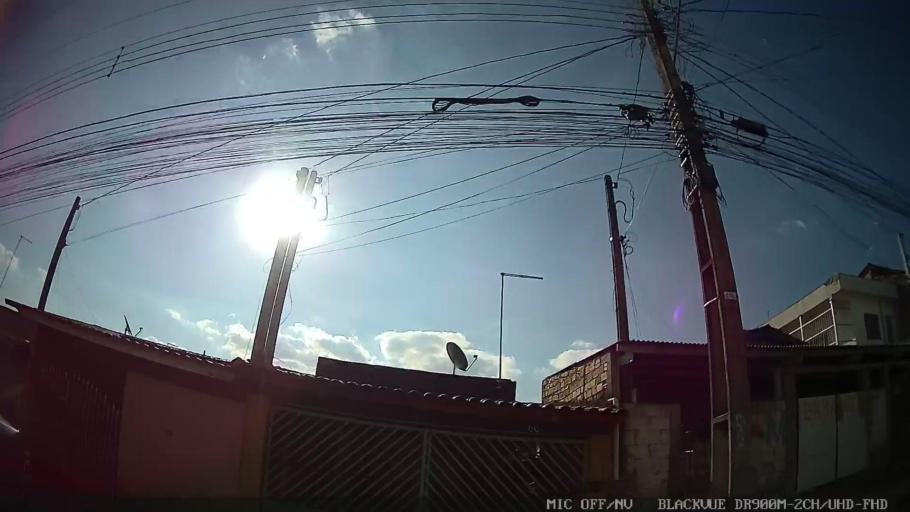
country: BR
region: Sao Paulo
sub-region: Cabreuva
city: Cabreuva
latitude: -23.2561
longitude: -47.0600
